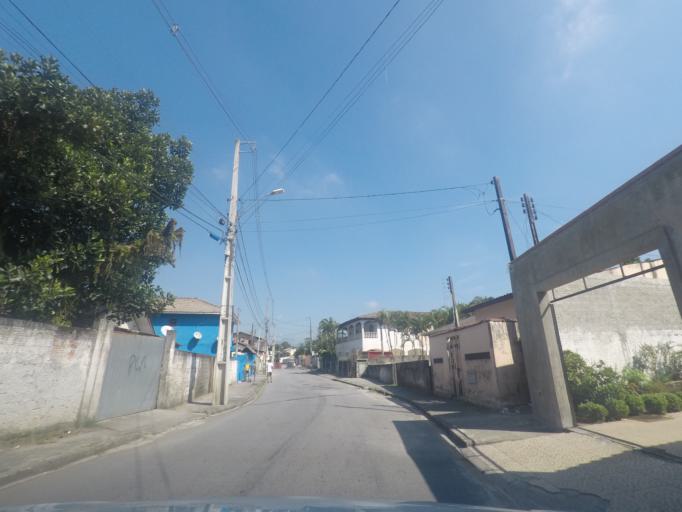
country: BR
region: Parana
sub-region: Paranagua
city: Paranagua
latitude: -25.5297
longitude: -48.5169
